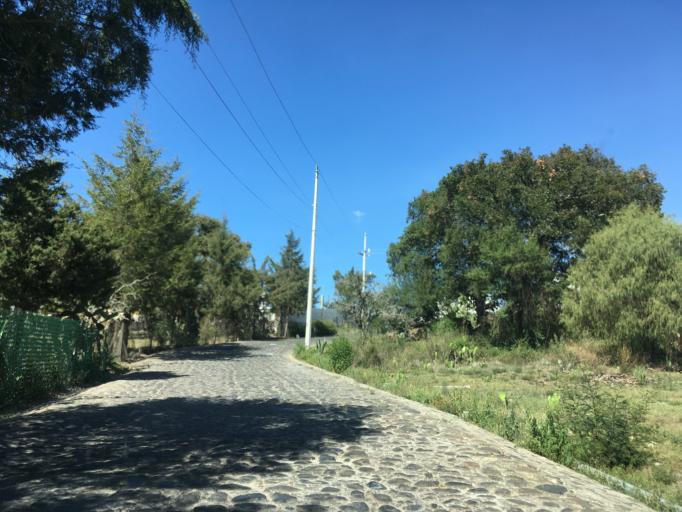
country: MX
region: Hidalgo
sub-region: Omitlan de Juarez
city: San Antonio el Paso
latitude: 20.2323
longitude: -98.5557
